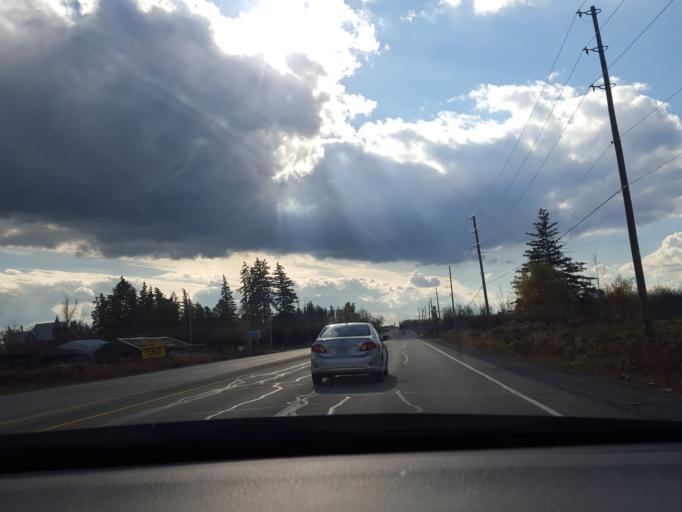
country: CA
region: Ontario
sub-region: Halton
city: Milton
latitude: 43.5481
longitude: -79.8162
